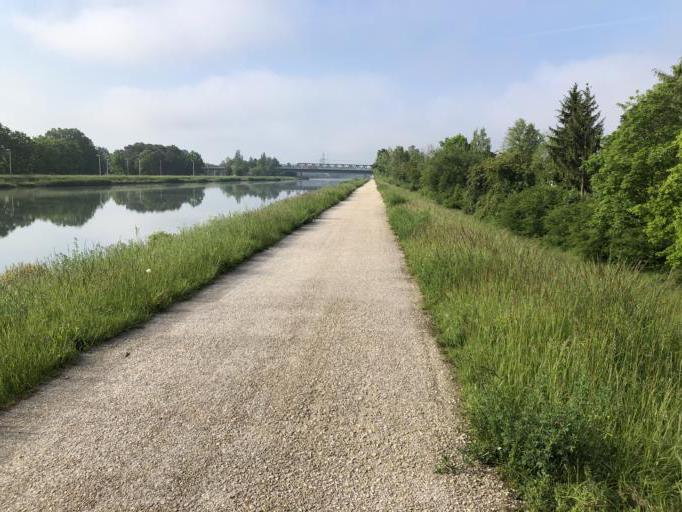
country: DE
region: Bavaria
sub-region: Regierungsbezirk Mittelfranken
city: Erlangen
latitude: 49.5700
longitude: 10.9703
